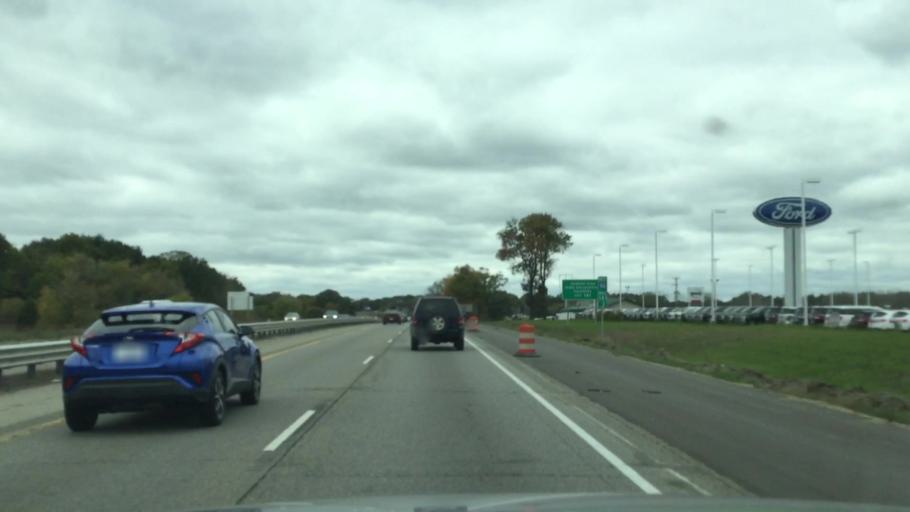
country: US
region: Michigan
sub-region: Jackson County
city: Jackson
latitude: 42.2766
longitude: -84.3726
